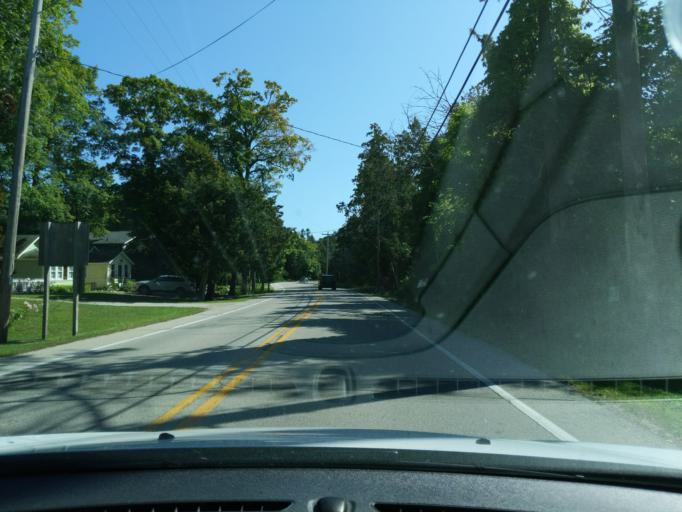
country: US
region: Michigan
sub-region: Delta County
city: Escanaba
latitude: 45.2898
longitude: -87.0221
